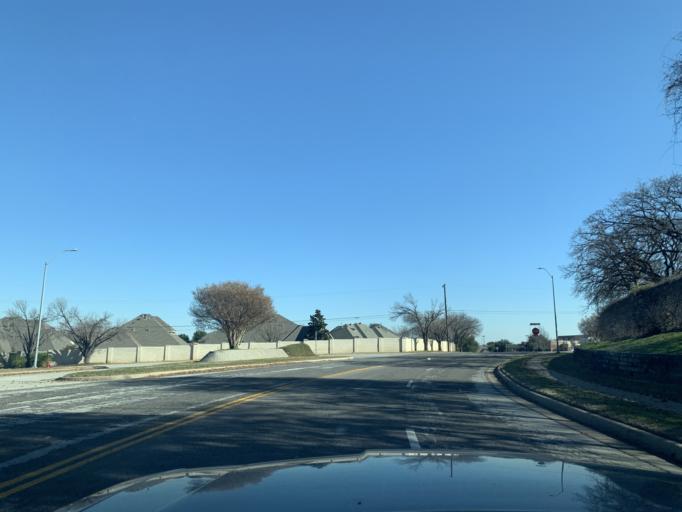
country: US
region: Texas
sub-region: Tarrant County
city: Bedford
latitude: 32.8418
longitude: -97.1381
